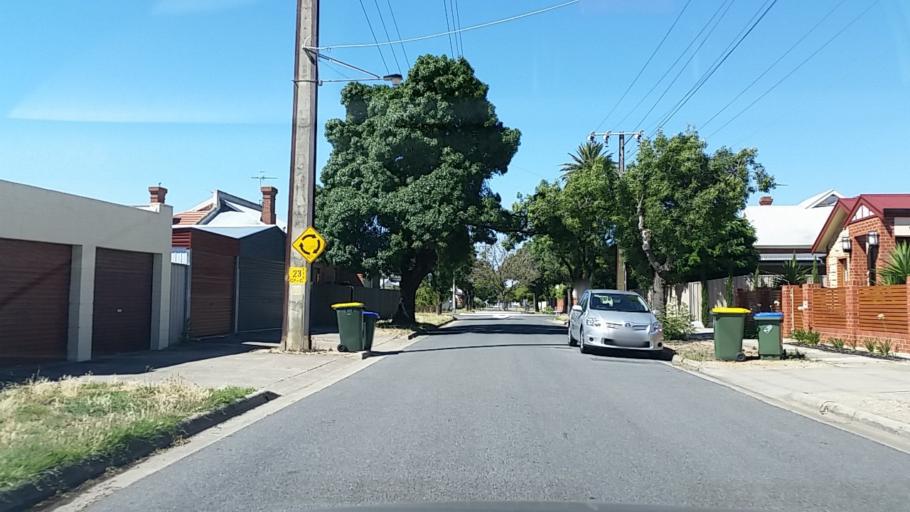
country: AU
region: South Australia
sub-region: Charles Sturt
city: Allenby Gardens
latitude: -34.8930
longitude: 138.5611
